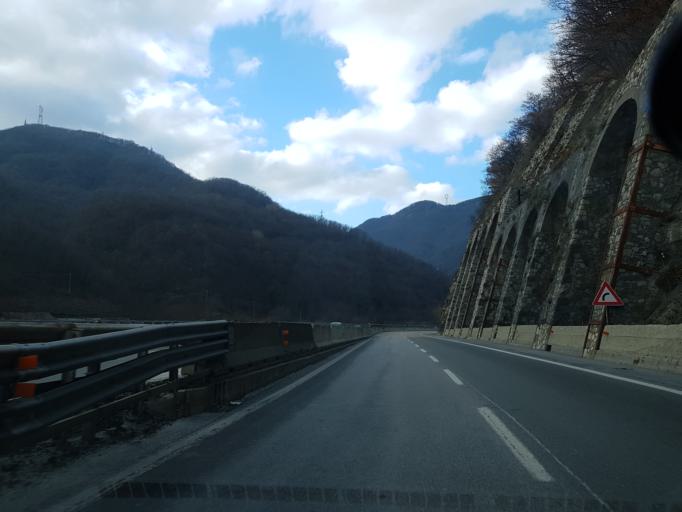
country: IT
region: Liguria
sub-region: Provincia di Genova
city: Ronco Scrivia
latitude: 44.6274
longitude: 8.9458
